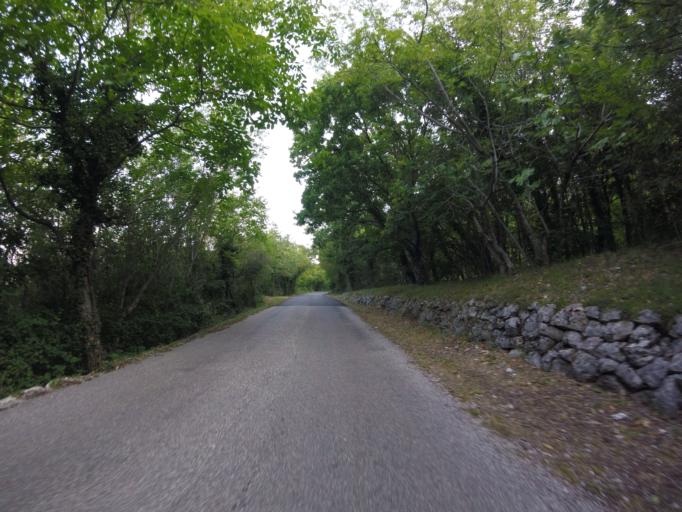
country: HR
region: Primorsko-Goranska
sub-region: Grad Crikvenica
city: Crikvenica
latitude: 45.2131
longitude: 14.7103
